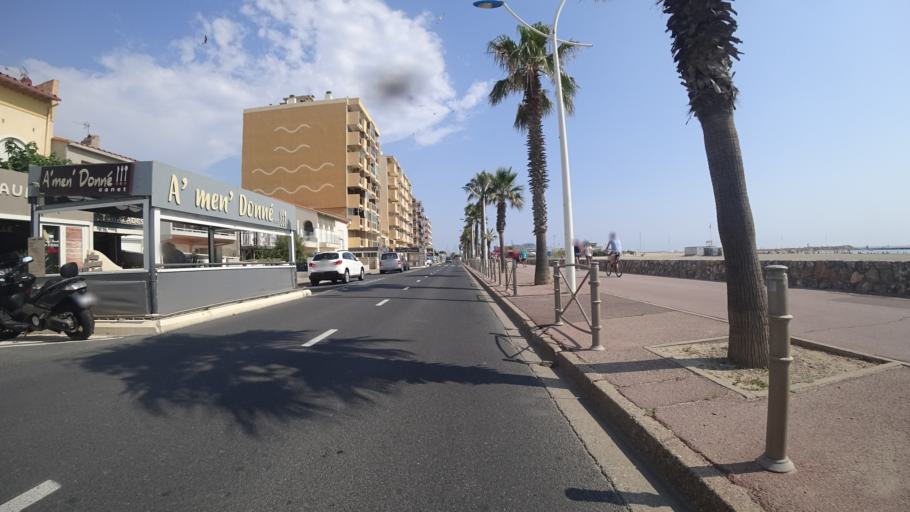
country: FR
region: Languedoc-Roussillon
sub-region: Departement des Pyrenees-Orientales
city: Canet-en-Roussillon
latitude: 42.6996
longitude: 3.0364
